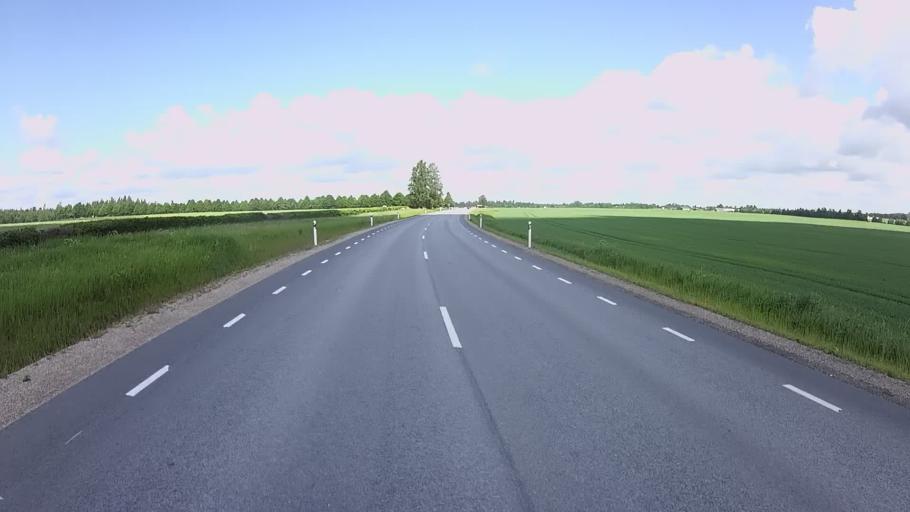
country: EE
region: Viljandimaa
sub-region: Viiratsi vald
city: Viiratsi
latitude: 58.3434
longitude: 25.6272
